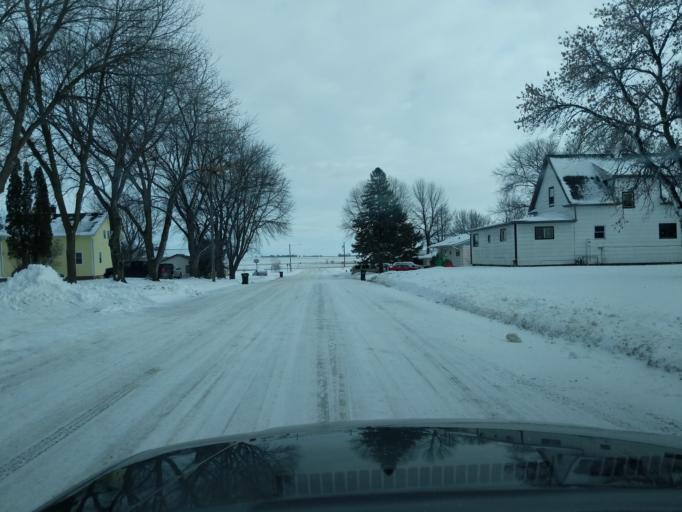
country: US
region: Minnesota
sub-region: Renville County
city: Renville
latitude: 44.7859
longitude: -95.3433
